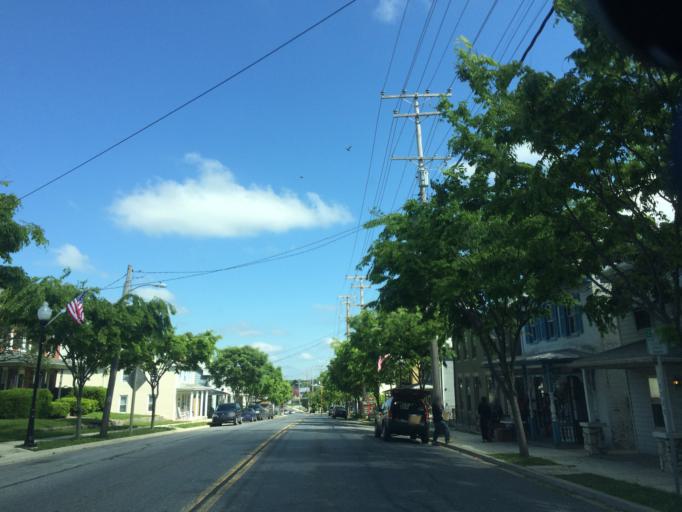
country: US
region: Maryland
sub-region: Carroll County
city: Manchester
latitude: 39.6623
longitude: -76.8853
